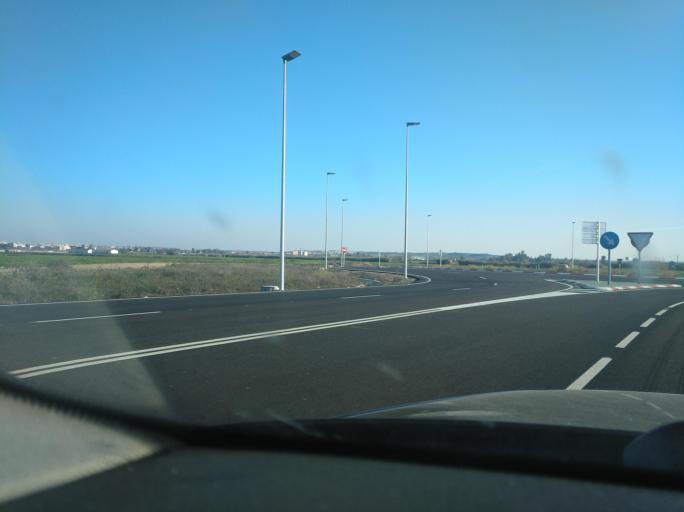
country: ES
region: Extremadura
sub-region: Provincia de Badajoz
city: Badajoz
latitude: 38.8764
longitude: -7.0255
